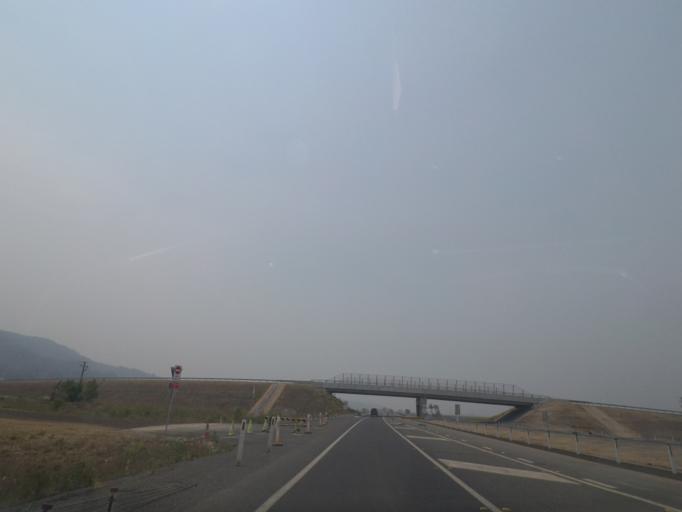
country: AU
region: New South Wales
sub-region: Ballina
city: Ballina
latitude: -28.9033
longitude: 153.4793
